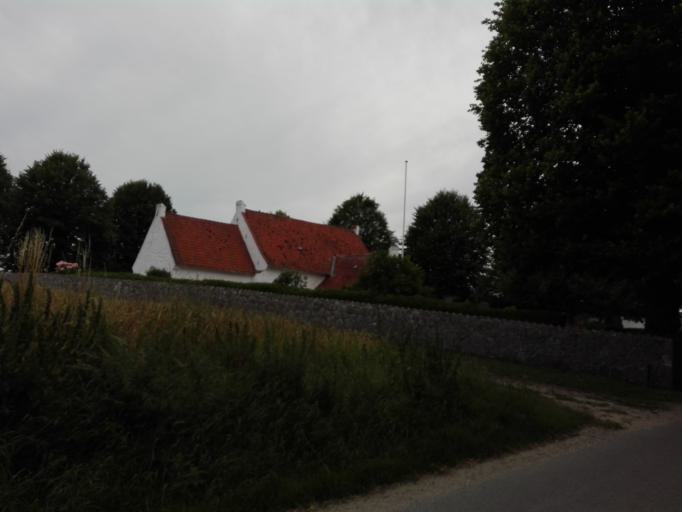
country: DK
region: Central Jutland
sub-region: Odder Kommune
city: Odder
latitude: 55.8571
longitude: 10.0760
